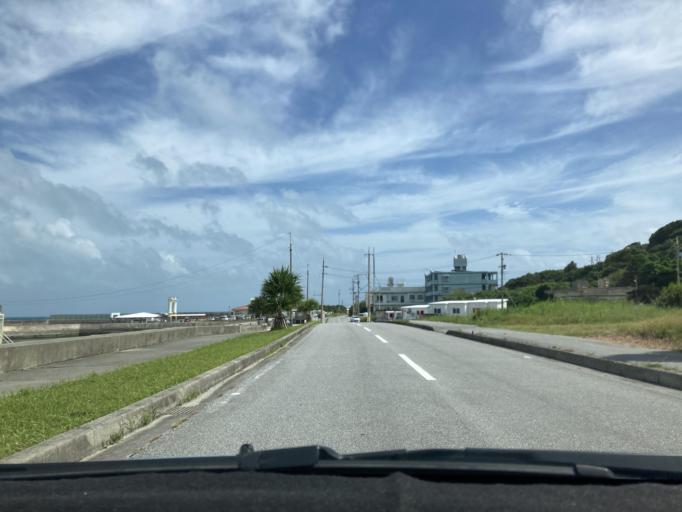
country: JP
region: Okinawa
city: Ginowan
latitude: 26.1794
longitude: 127.8242
